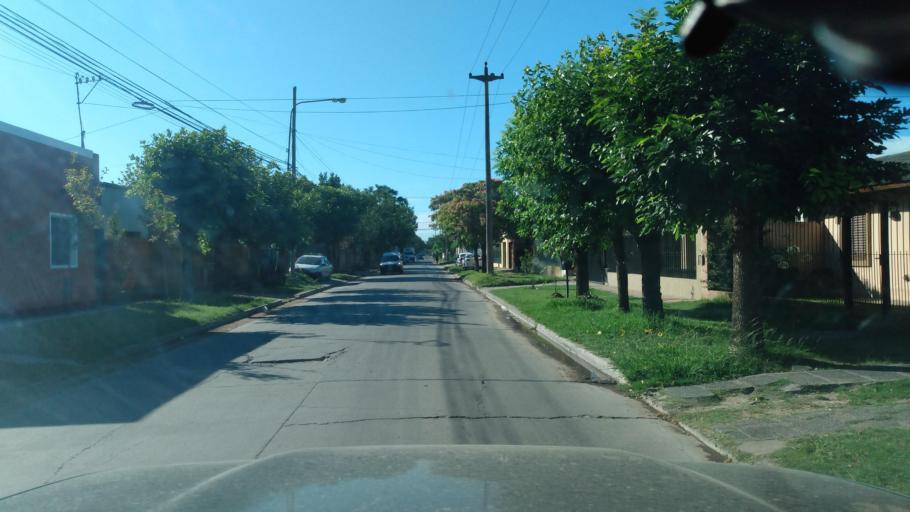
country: AR
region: Buenos Aires
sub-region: Partido de Lujan
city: Lujan
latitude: -34.5693
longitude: -59.0907
